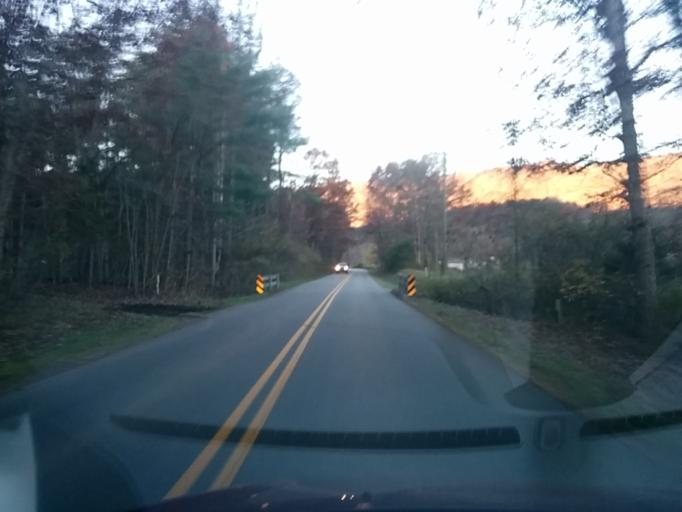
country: US
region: Virginia
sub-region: City of Lexington
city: Lexington
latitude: 37.9528
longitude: -79.5465
